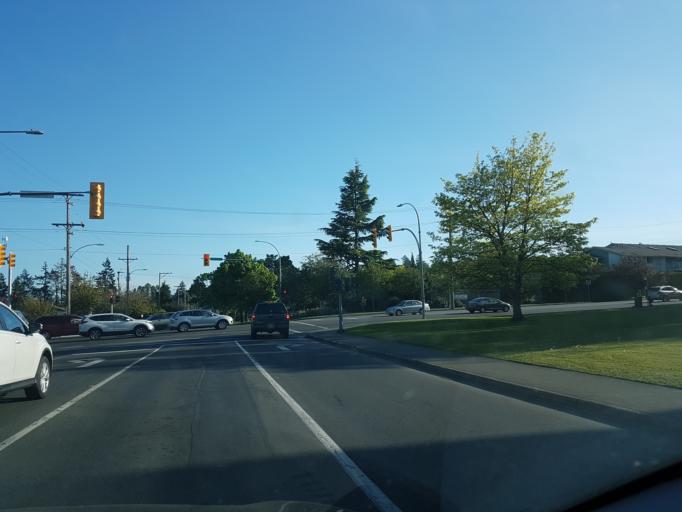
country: CA
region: British Columbia
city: Oak Bay
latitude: 48.4690
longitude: -123.3353
